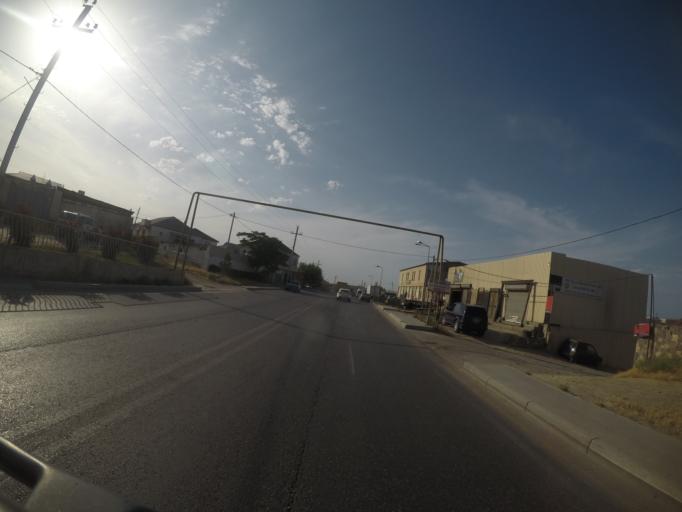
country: AZ
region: Baki
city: Binagadi
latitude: 40.4744
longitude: 49.8340
